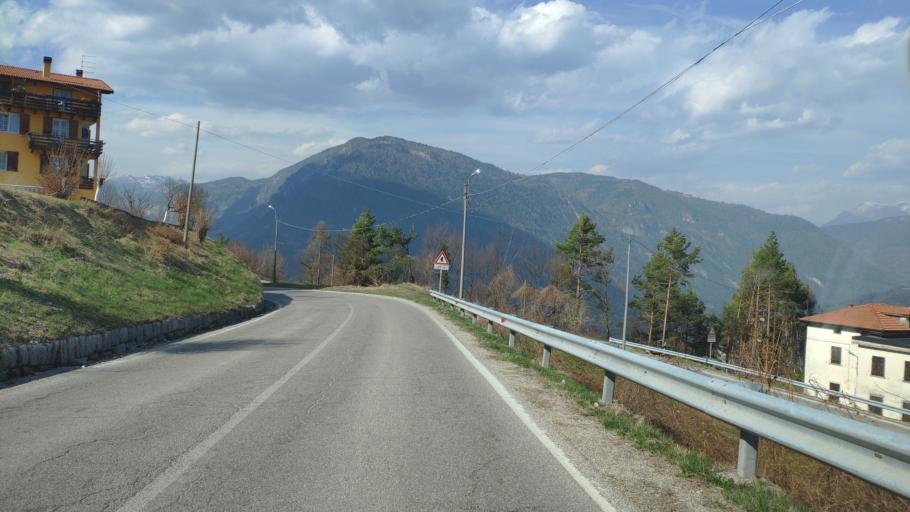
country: IT
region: Veneto
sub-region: Provincia di Vicenza
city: Enego
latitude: 45.9486
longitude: 11.7073
